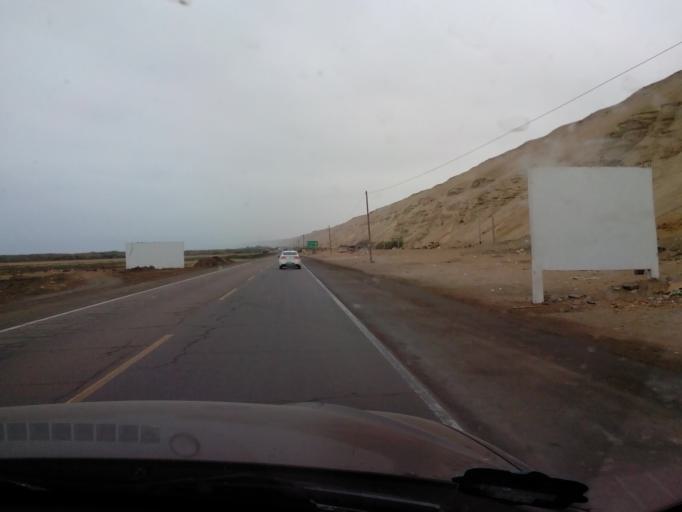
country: PE
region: Ica
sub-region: Provincia de Chincha
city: Sunampe
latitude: -13.4096
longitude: -76.1907
